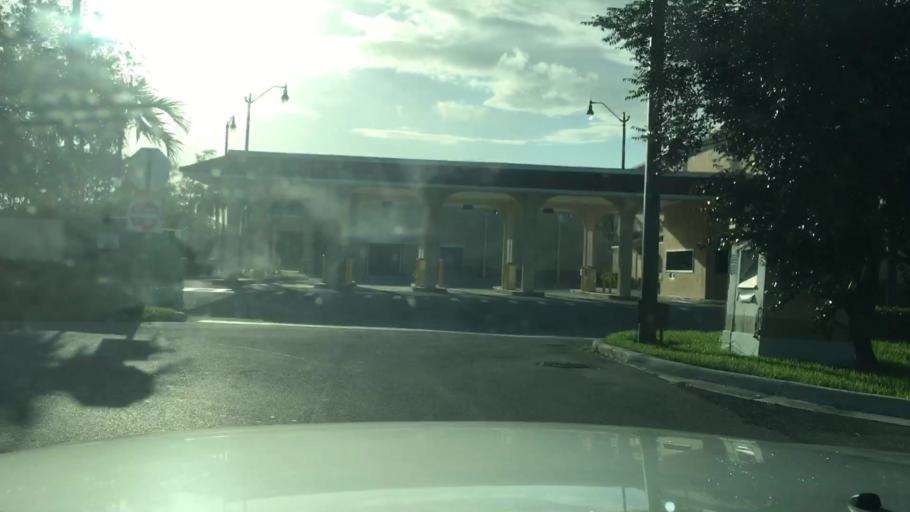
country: US
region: Florida
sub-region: Miami-Dade County
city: Leisure City
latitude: 25.4766
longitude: -80.4348
